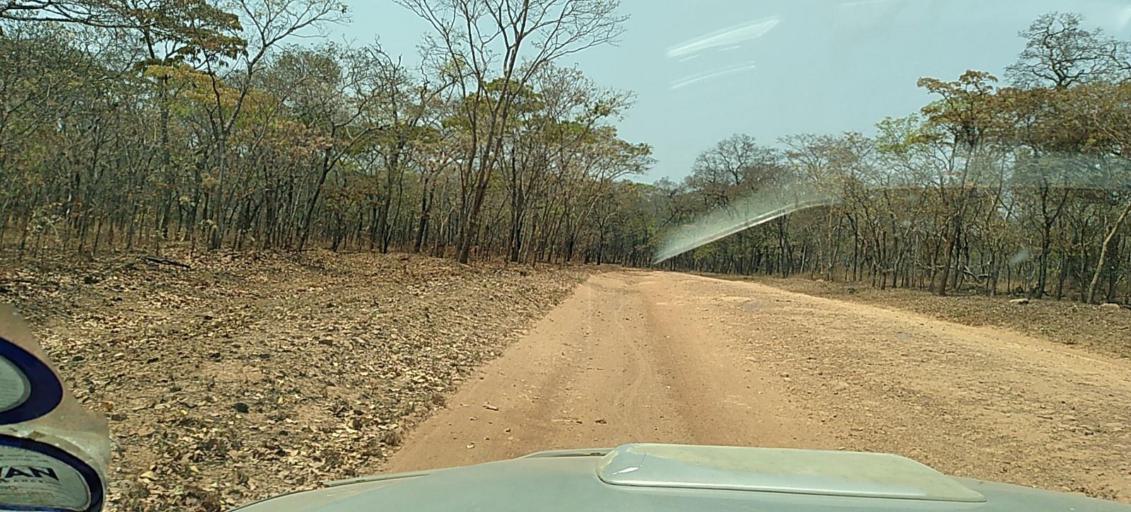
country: ZM
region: North-Western
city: Kasempa
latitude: -13.5555
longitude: 26.0691
